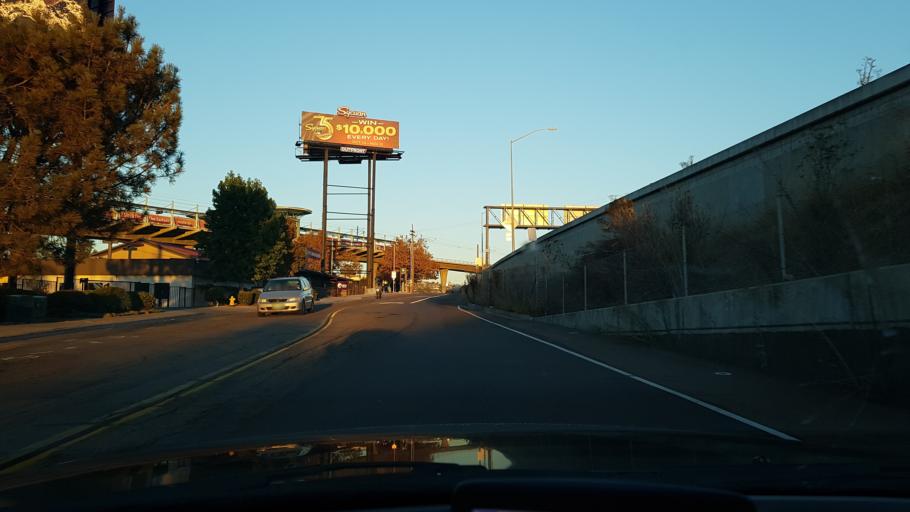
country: US
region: California
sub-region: San Diego County
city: La Mesa
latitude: 32.7799
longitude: -117.0992
